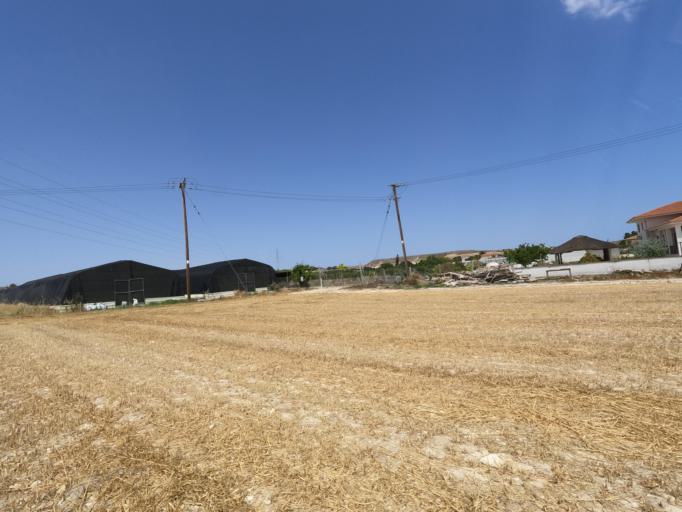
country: CY
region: Larnaka
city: Voroklini
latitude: 34.9874
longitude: 33.6767
